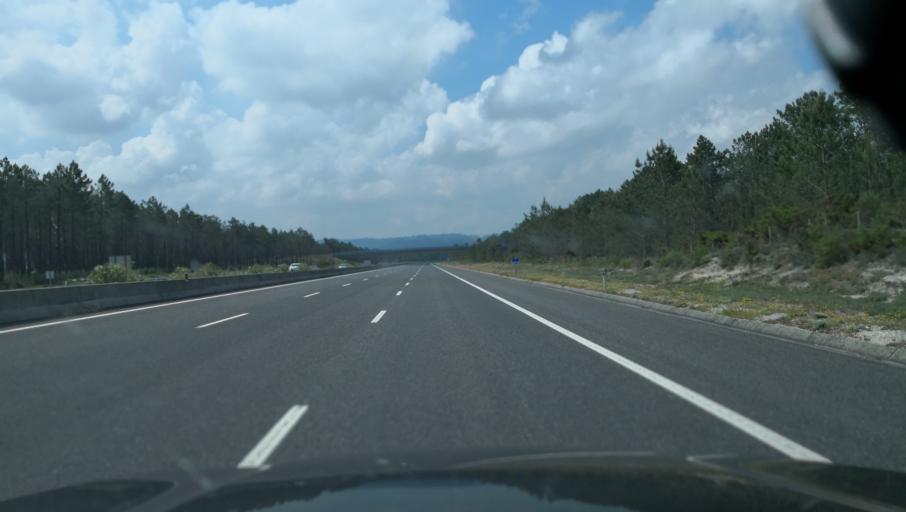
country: PT
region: Leiria
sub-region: Alcobaca
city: Alcobaca
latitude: 39.6035
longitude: -9.0007
